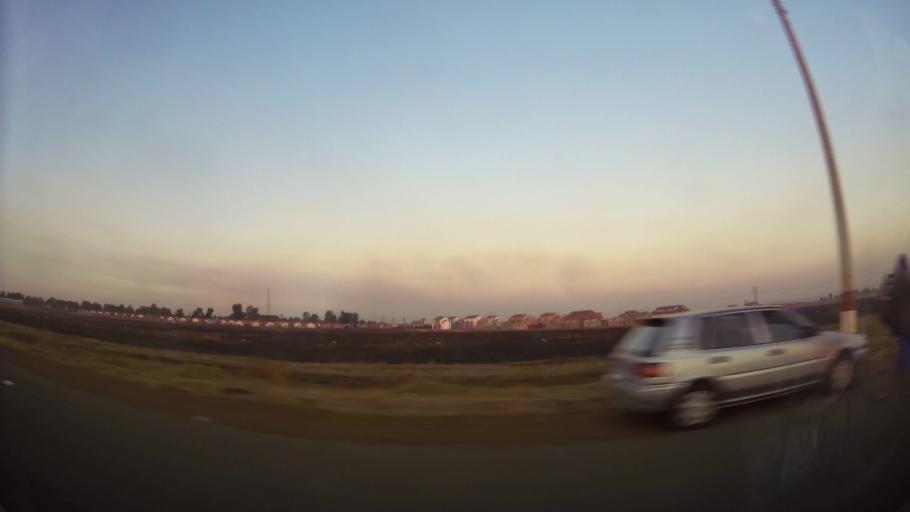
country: ZA
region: Gauteng
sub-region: Ekurhuleni Metropolitan Municipality
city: Springs
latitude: -26.3156
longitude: 28.4254
